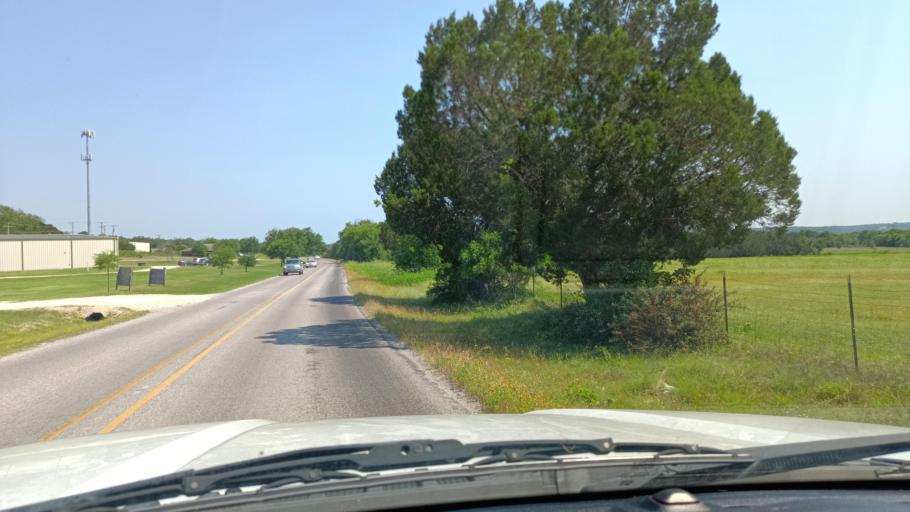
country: US
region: Texas
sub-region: Bell County
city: Morgans Point Resort
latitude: 31.1037
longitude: -97.5197
